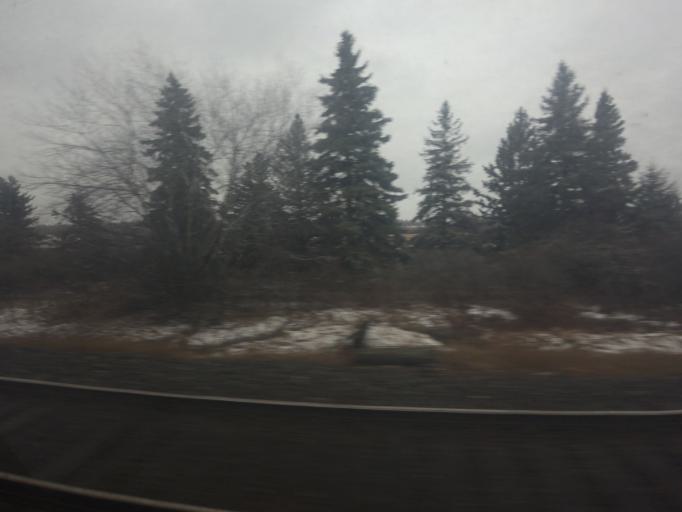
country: CA
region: Ontario
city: Kingston
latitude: 44.3057
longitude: -76.4053
